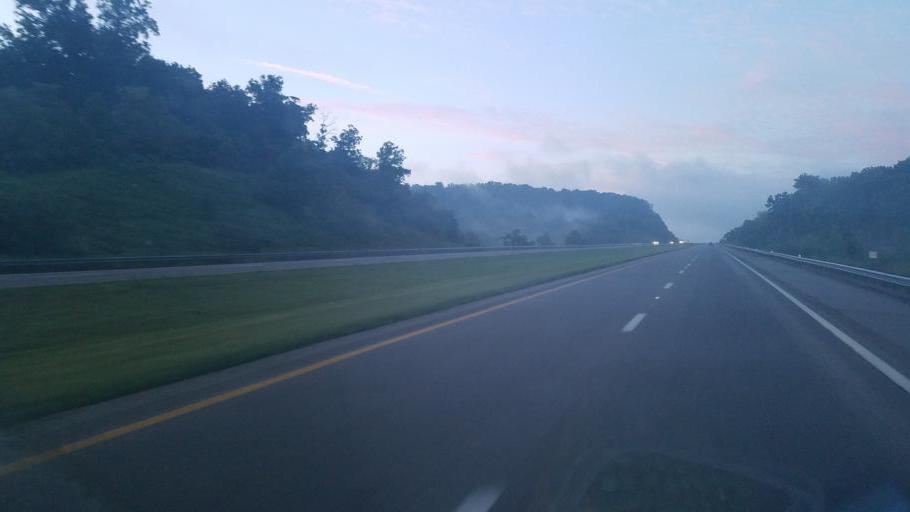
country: US
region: Ohio
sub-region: Ross County
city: Chillicothe
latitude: 39.2391
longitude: -82.8395
